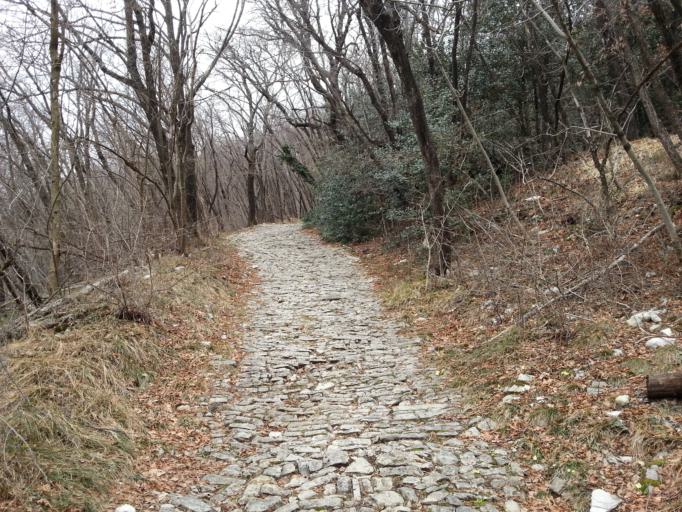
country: CH
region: Ticino
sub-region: Mendrisio District
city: Riva San Vitale
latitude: 45.8987
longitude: 8.9500
